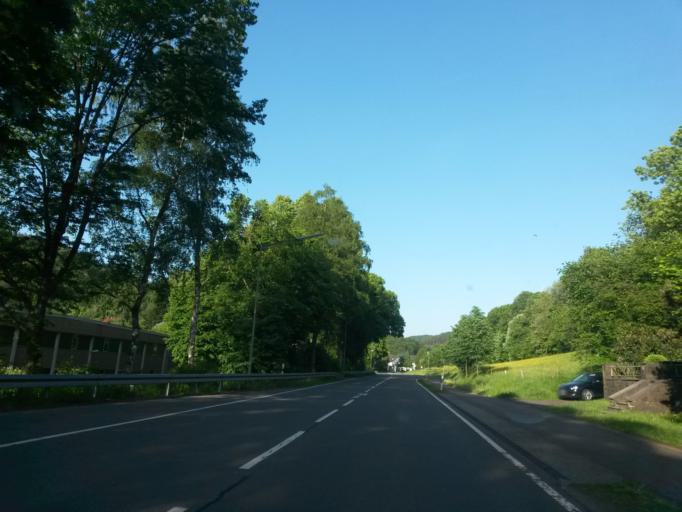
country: DE
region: North Rhine-Westphalia
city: Bergneustadt
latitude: 51.0402
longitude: 7.7038
